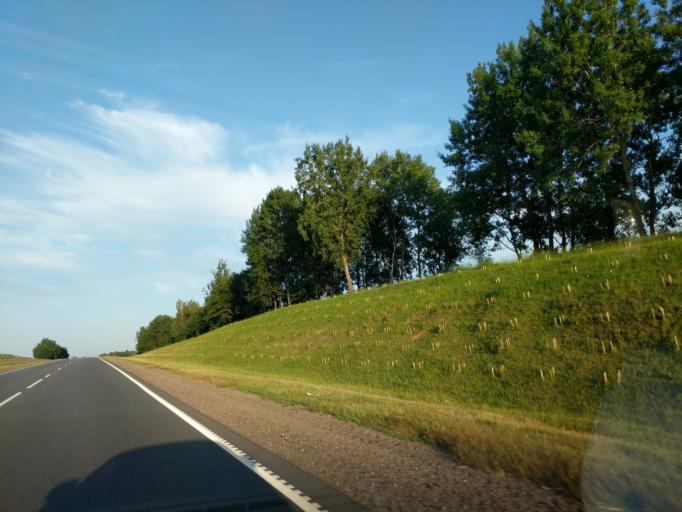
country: BY
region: Minsk
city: Bal'shavik
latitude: 54.0921
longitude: 27.5224
